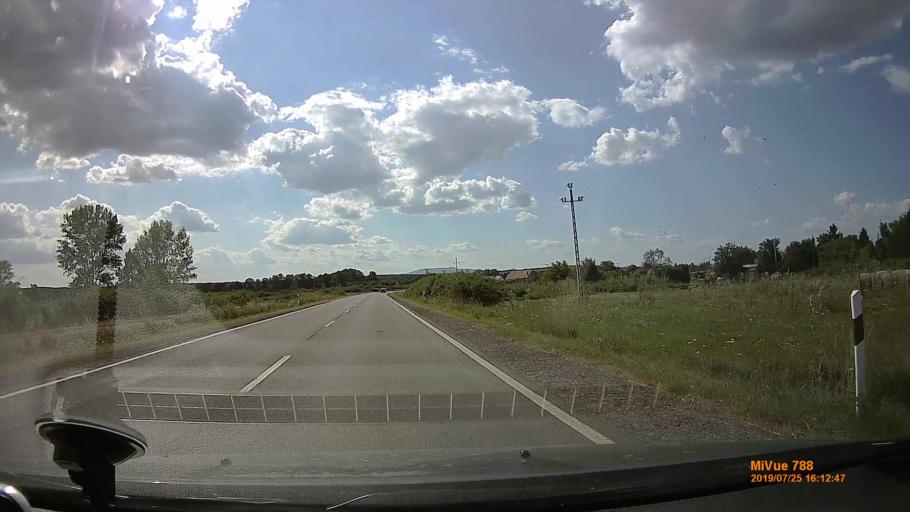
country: HU
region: Heves
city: Kerecsend
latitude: 47.7879
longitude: 20.3491
